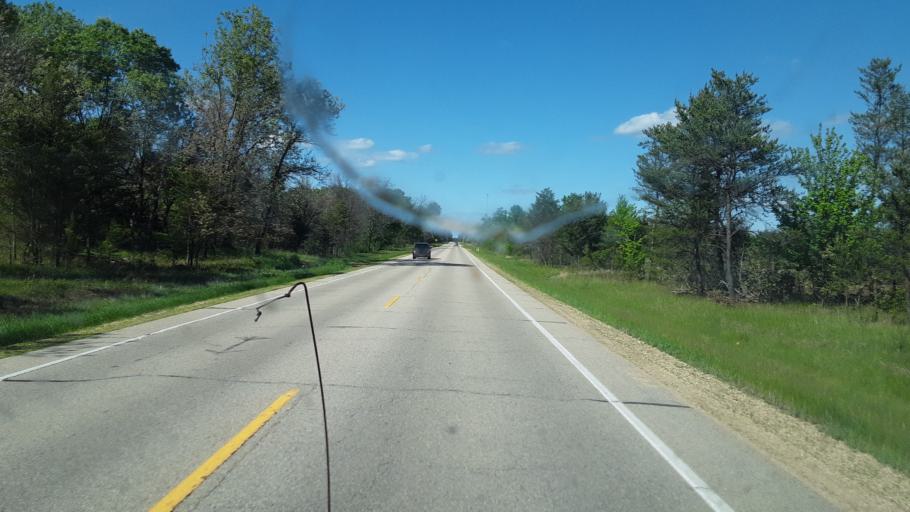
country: US
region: Wisconsin
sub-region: Juneau County
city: New Lisbon
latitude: 43.9530
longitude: -90.0876
